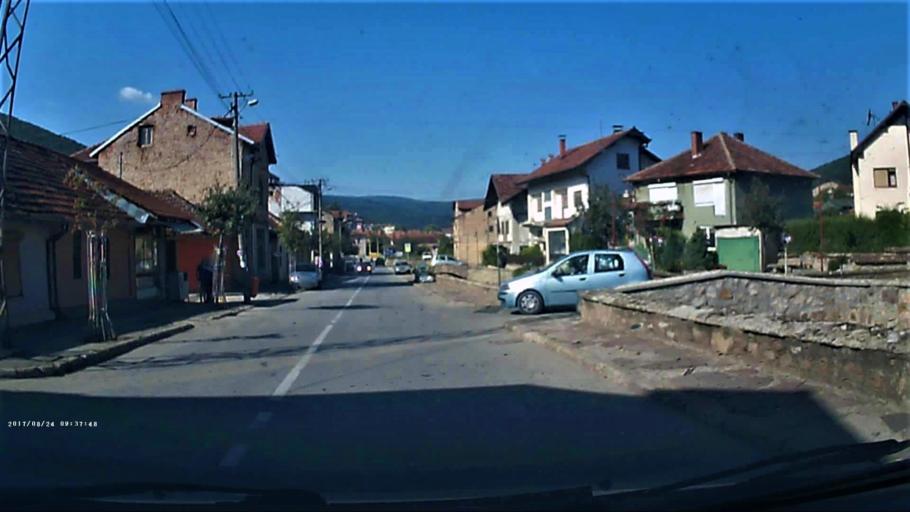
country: RS
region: Central Serbia
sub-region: Pirotski Okrug
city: Dimitrovgrad
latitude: 43.0182
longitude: 22.7813
